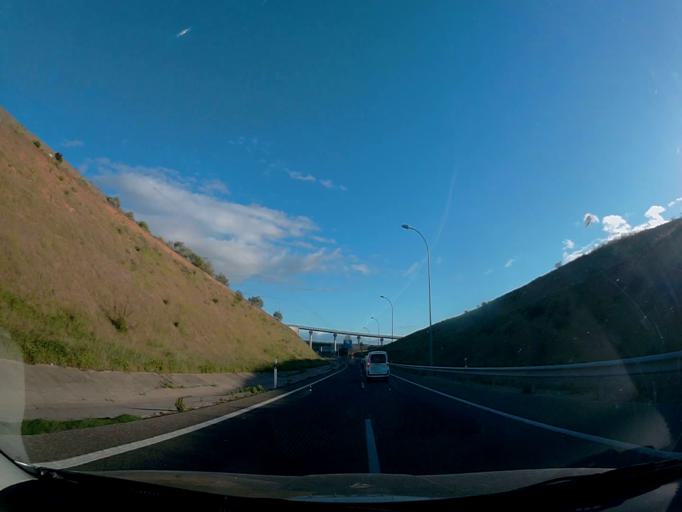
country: ES
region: Madrid
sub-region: Provincia de Madrid
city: Ajalvir
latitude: 40.5068
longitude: -3.4943
